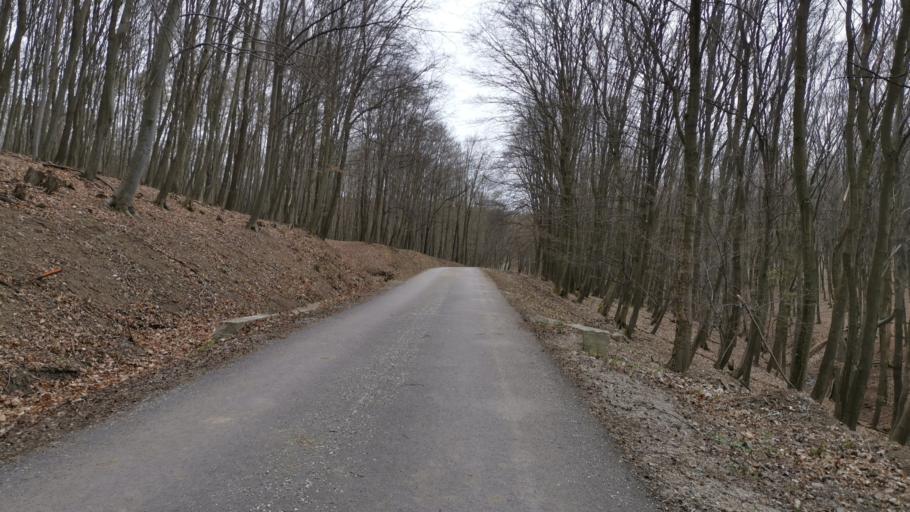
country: CZ
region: South Moravian
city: Petrov
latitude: 48.8116
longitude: 17.3233
